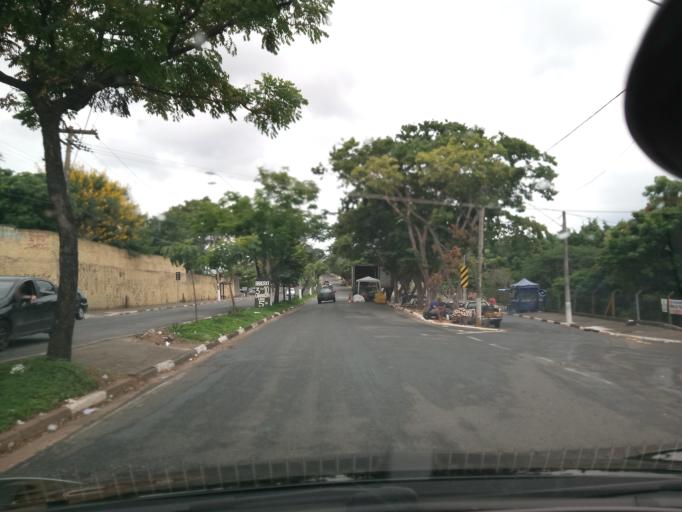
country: BR
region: Sao Paulo
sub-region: Campinas
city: Campinas
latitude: -22.9750
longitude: -47.1283
